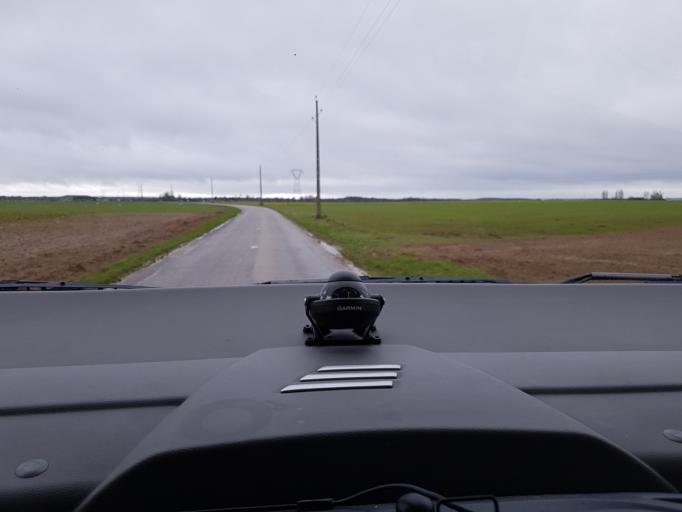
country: FR
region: Haute-Normandie
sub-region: Departement de l'Eure
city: Pont-Saint-Pierre
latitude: 49.2985
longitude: 1.3291
